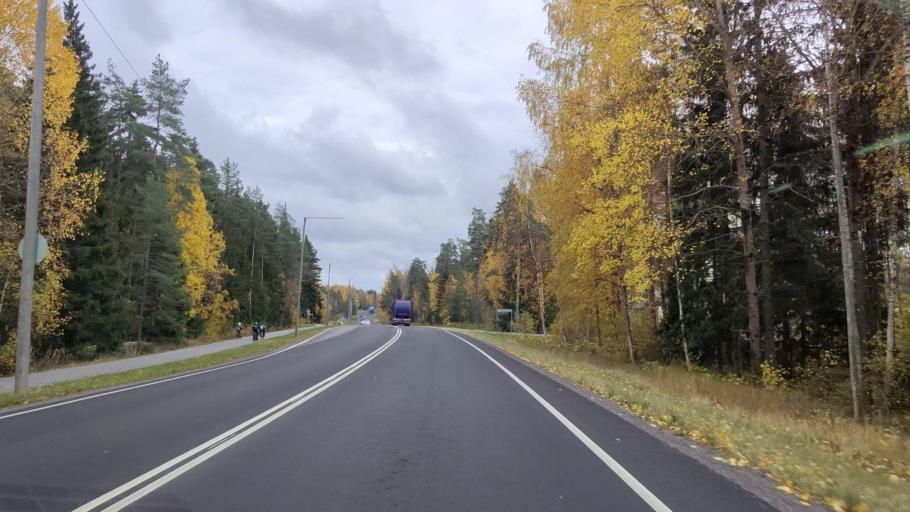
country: FI
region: Varsinais-Suomi
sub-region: Turku
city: Kaarina
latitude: 60.4562
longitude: 22.3668
